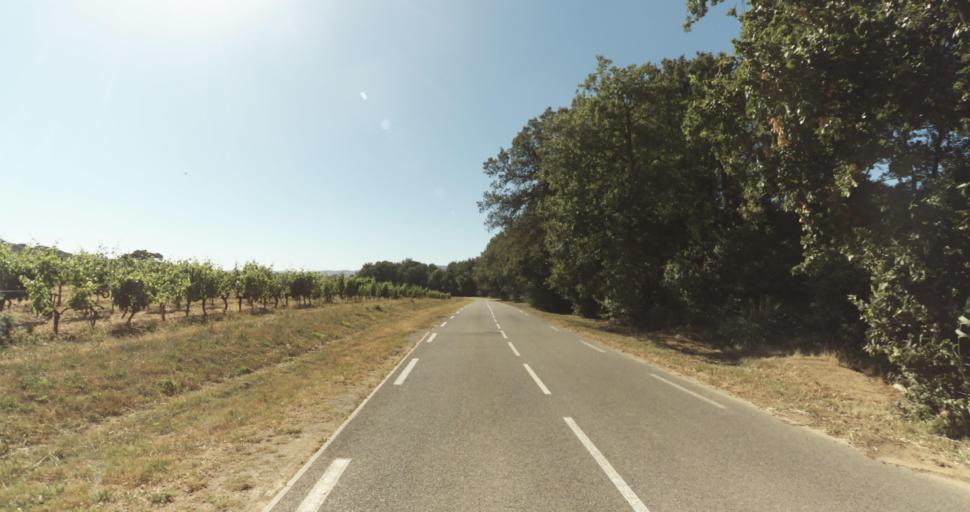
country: FR
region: Provence-Alpes-Cote d'Azur
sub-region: Departement du Var
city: Gassin
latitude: 43.2522
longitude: 6.5973
